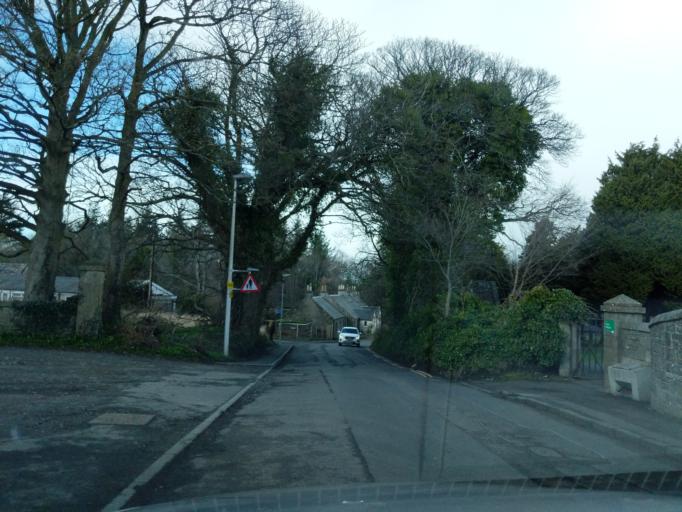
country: GB
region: Scotland
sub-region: Edinburgh
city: Currie
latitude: 55.8945
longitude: -3.3084
